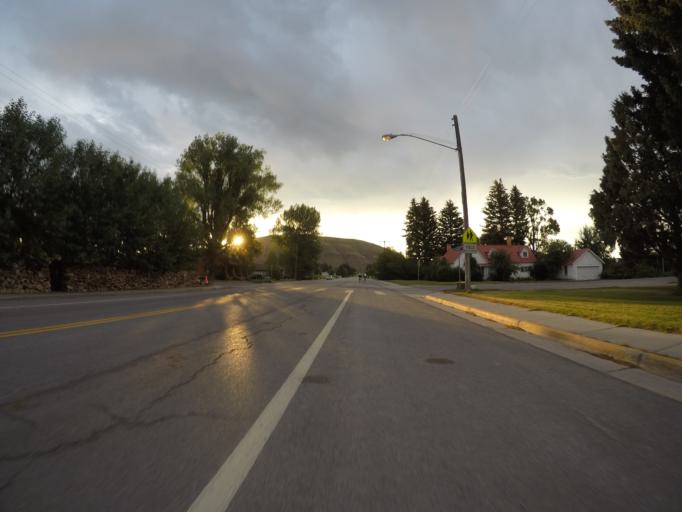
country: US
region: Idaho
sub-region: Bear Lake County
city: Montpelier
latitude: 42.0855
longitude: -110.9541
